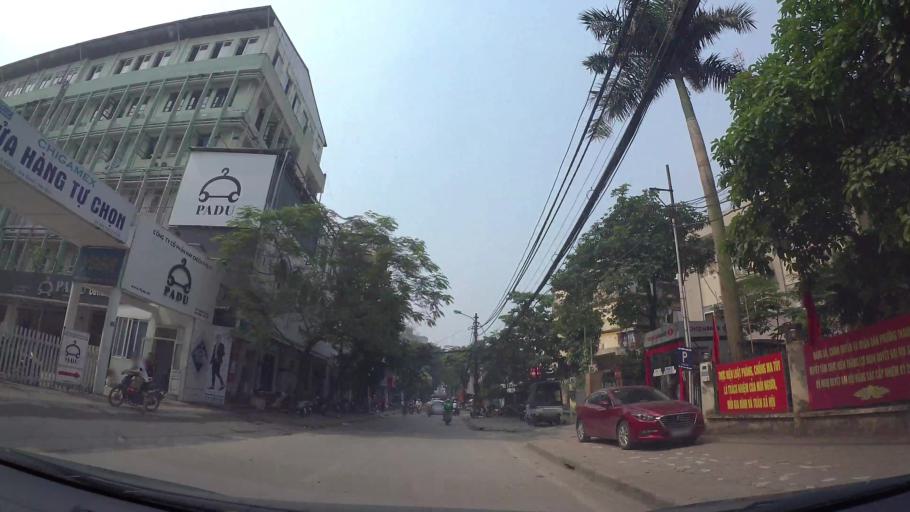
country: VN
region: Ha Noi
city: Dong Da
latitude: 21.0224
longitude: 105.8160
